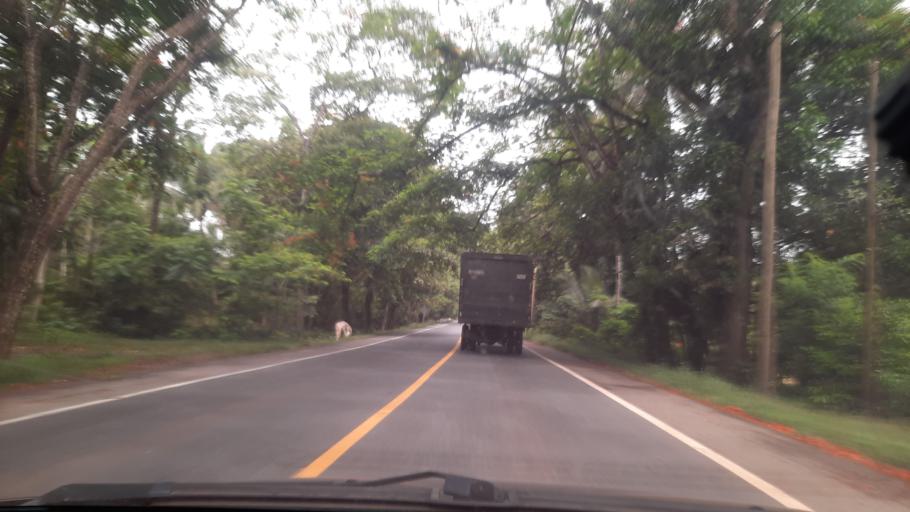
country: GT
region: Izabal
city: Morales
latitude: 15.4641
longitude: -88.9177
